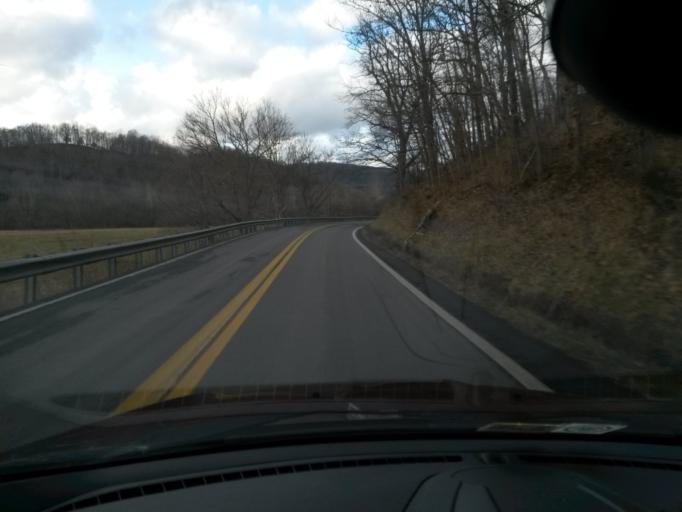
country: US
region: West Virginia
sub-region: Monroe County
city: Union
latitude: 37.5536
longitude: -80.5731
